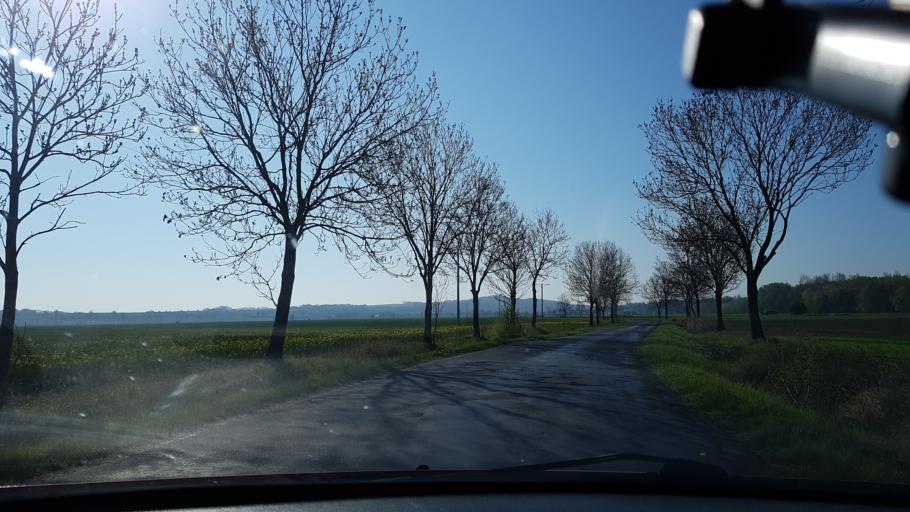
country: PL
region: Opole Voivodeship
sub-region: Powiat nyski
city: Nysa
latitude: 50.4237
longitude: 17.3145
